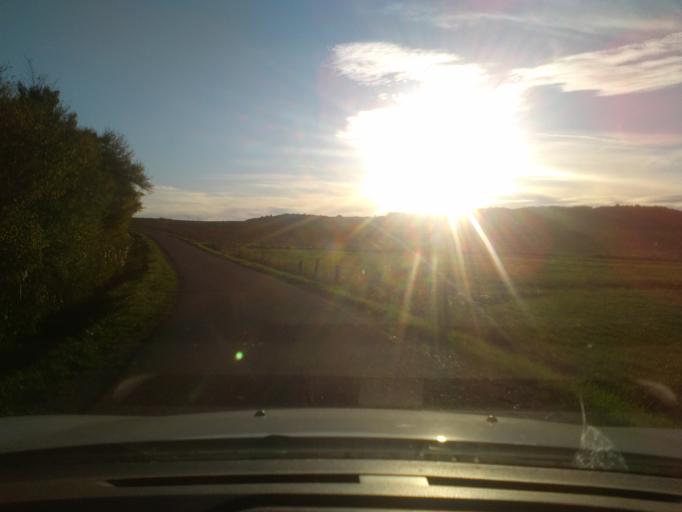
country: FR
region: Lorraine
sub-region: Departement des Vosges
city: Charmes
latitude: 48.3436
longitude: 6.2920
